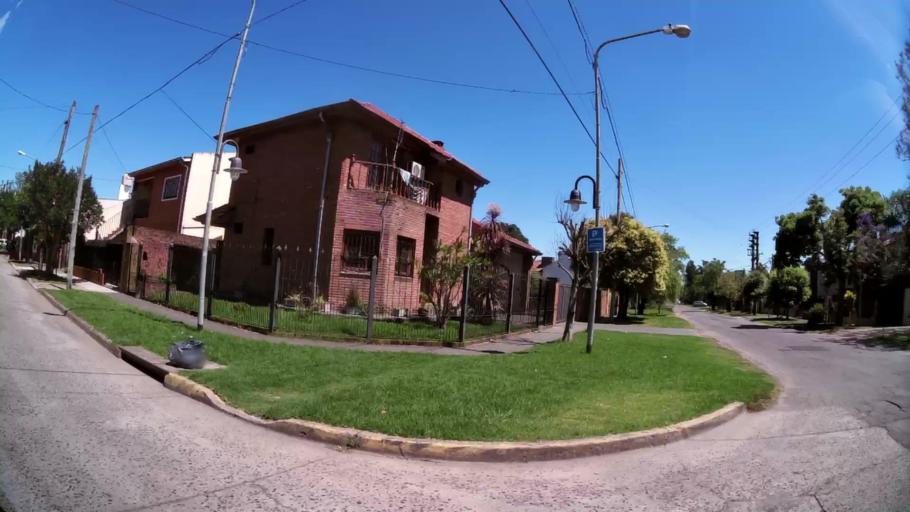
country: AR
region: Buenos Aires
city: Hurlingham
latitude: -34.5009
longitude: -58.6370
